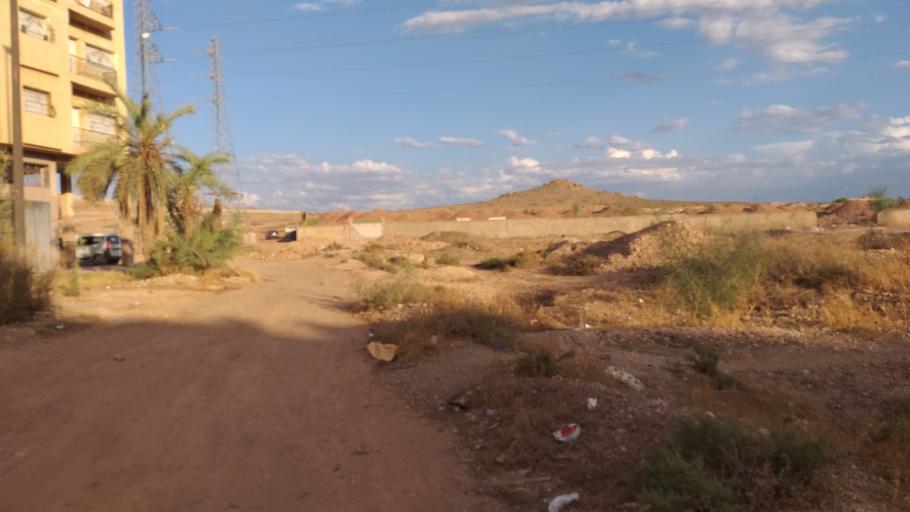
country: MA
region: Marrakech-Tensift-Al Haouz
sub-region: Marrakech
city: Marrakesh
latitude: 31.6674
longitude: -8.0222
